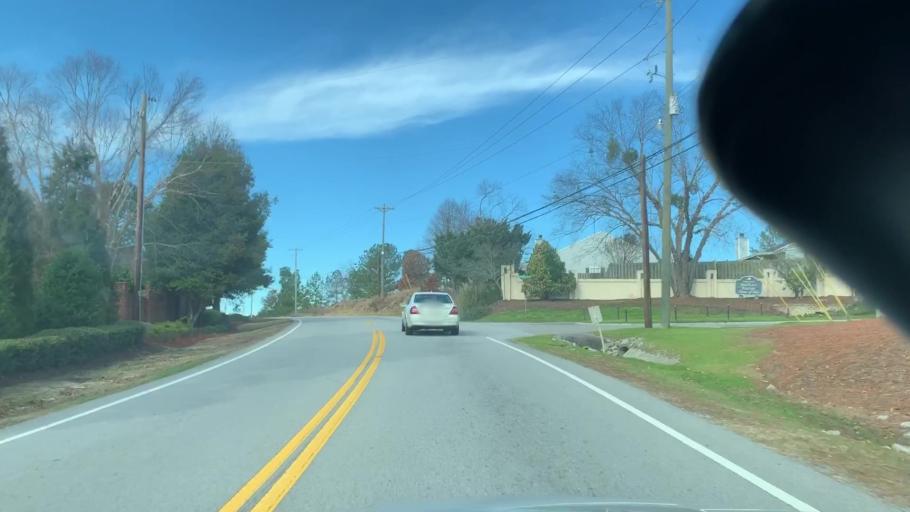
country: US
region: South Carolina
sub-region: Richland County
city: Woodfield
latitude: 34.1054
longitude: -80.8982
